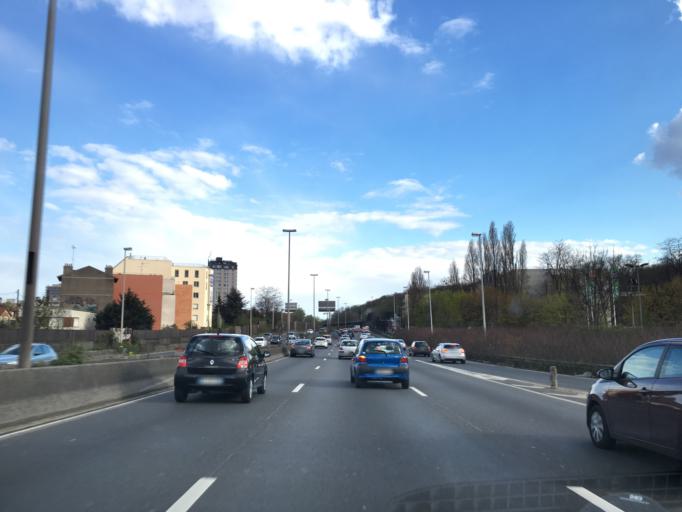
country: FR
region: Ile-de-France
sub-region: Departement de Seine-Saint-Denis
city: Noisy-le-Sec
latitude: 48.8763
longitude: 2.4779
